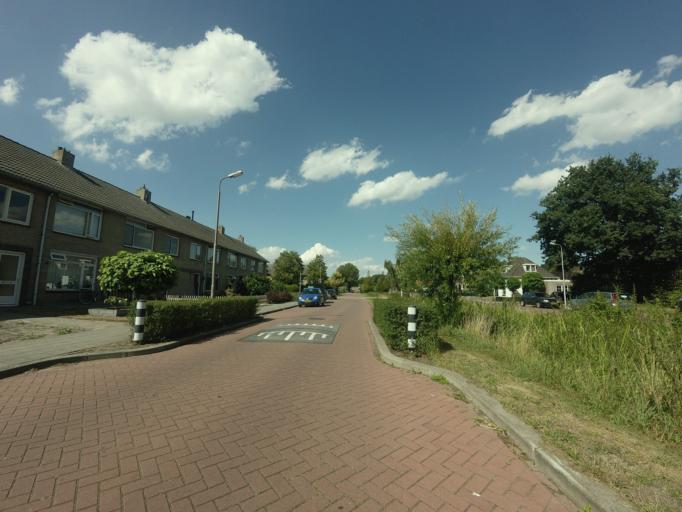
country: NL
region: Drenthe
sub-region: Gemeente Hoogeveen
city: Hoogeveen
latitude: 52.5968
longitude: 6.4598
